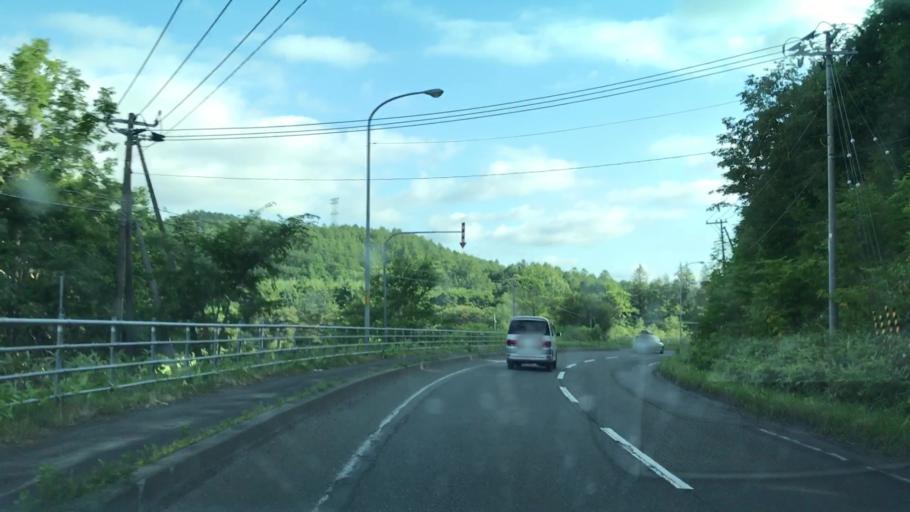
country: JP
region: Hokkaido
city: Shimo-furano
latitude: 42.8769
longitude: 142.1689
